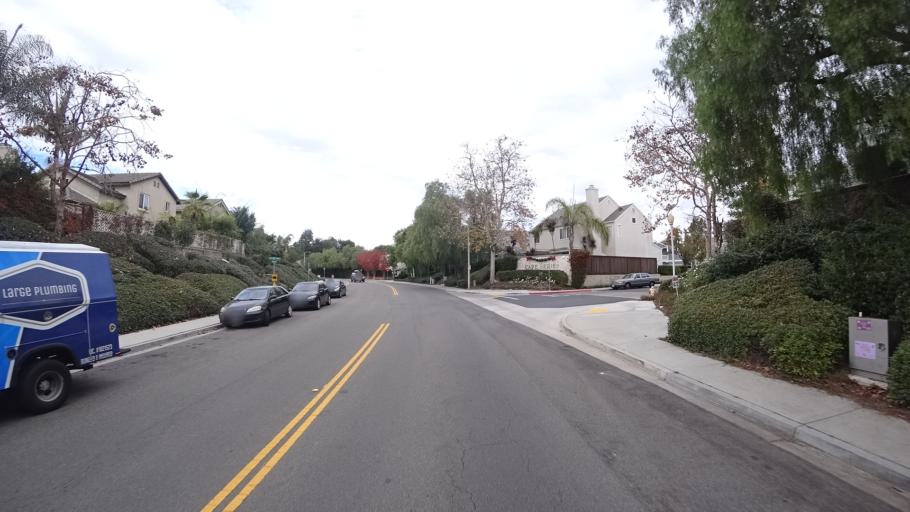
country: US
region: California
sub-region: Orange County
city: Aliso Viejo
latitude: 33.5673
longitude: -117.7325
